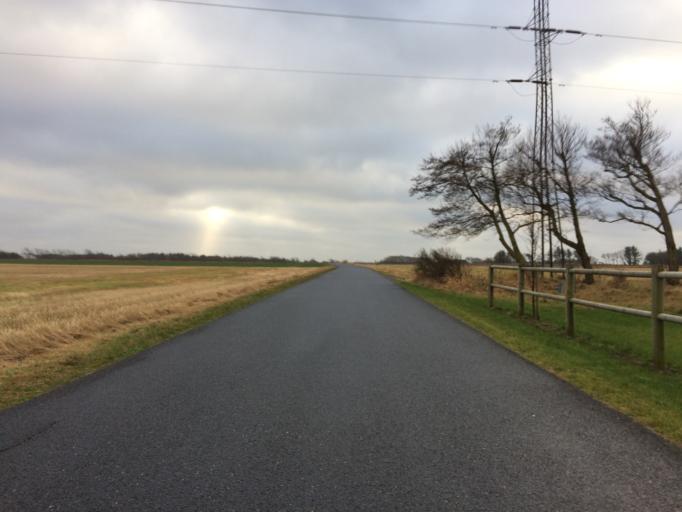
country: DK
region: Central Jutland
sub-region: Holstebro Kommune
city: Ulfborg
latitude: 56.2760
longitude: 8.2364
